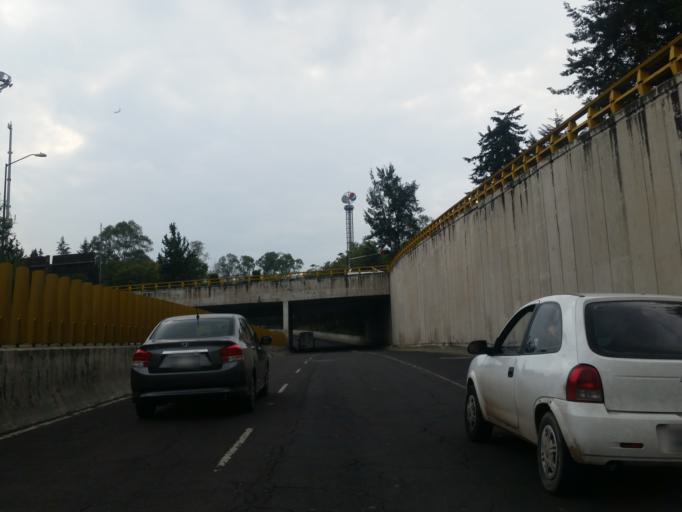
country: MX
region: Mexico City
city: Polanco
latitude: 19.4192
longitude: -99.1933
